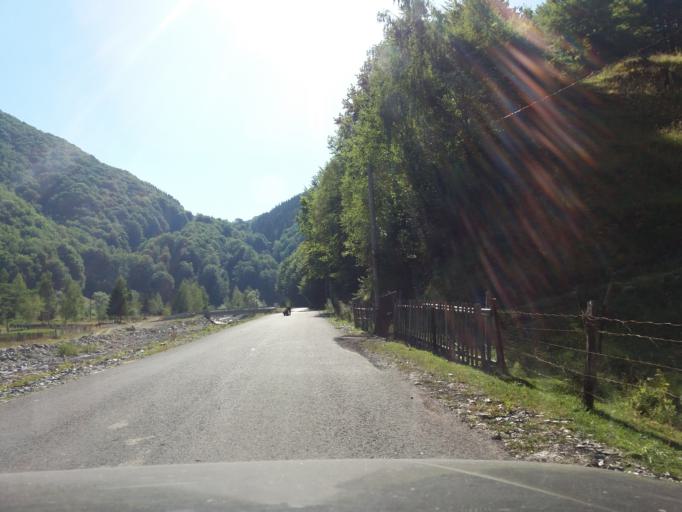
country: RO
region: Hunedoara
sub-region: Oras Petrila
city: Petrila
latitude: 45.4171
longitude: 23.4569
